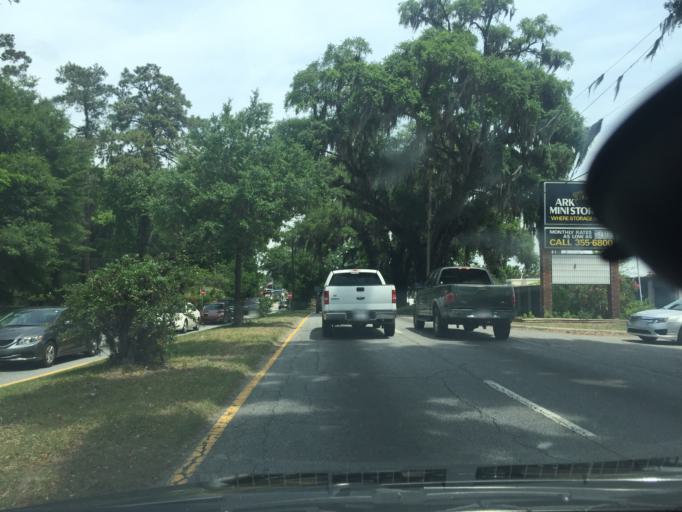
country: US
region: Georgia
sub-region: Chatham County
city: Savannah
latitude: 32.0261
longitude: -81.1118
